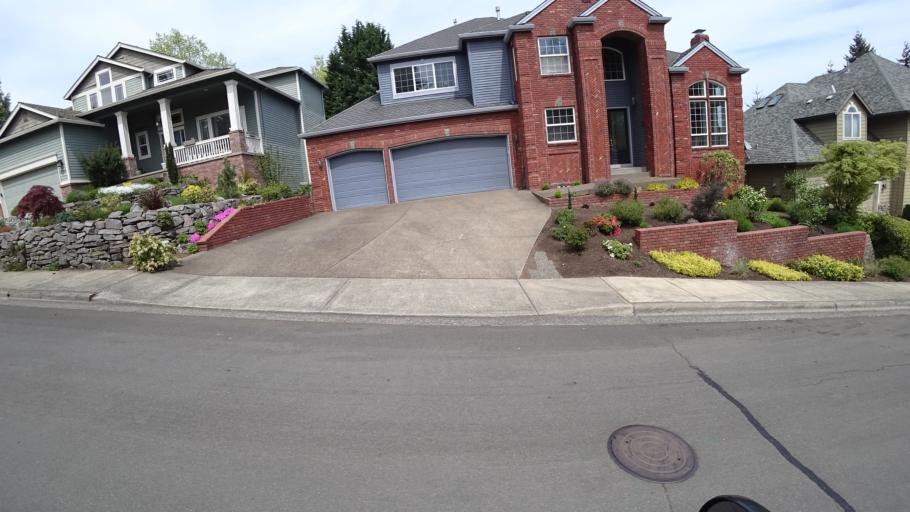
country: US
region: Oregon
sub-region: Washington County
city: Aloha
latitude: 45.4573
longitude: -122.8494
